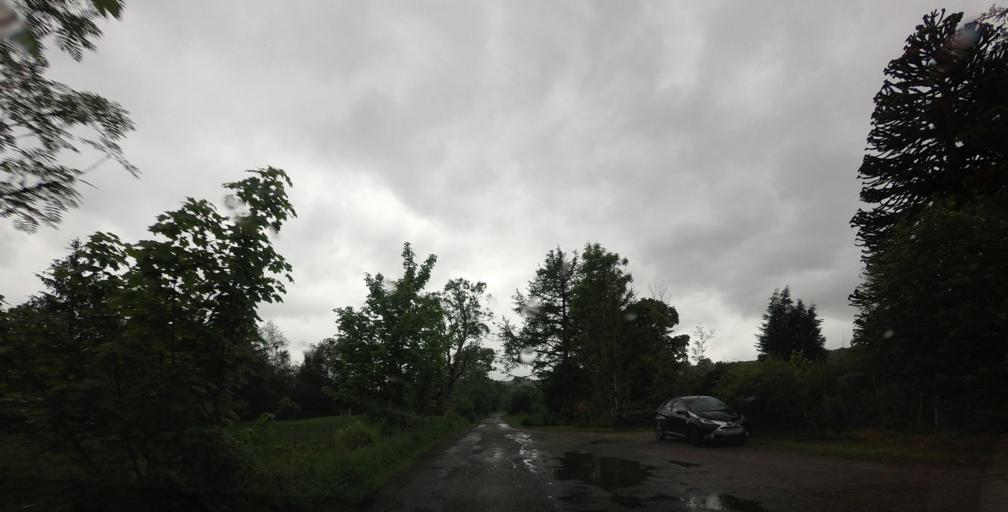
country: GB
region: Scotland
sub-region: Argyll and Bute
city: Oban
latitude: 56.7080
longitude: -5.5630
